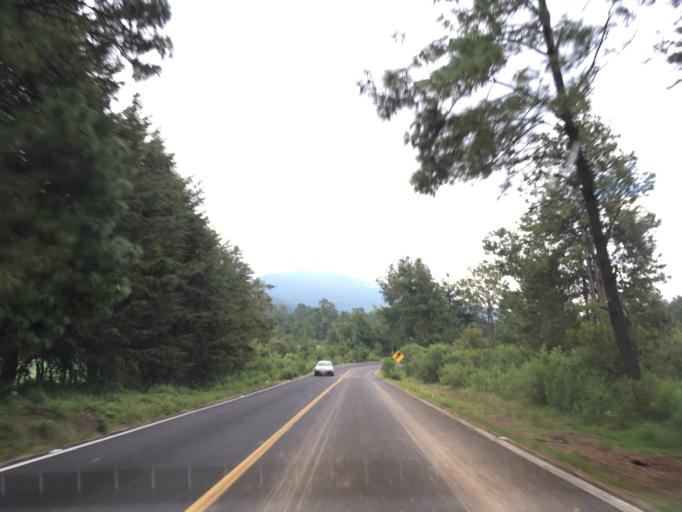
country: MX
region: Michoacan
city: Pichataro
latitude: 19.5875
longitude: -101.8303
